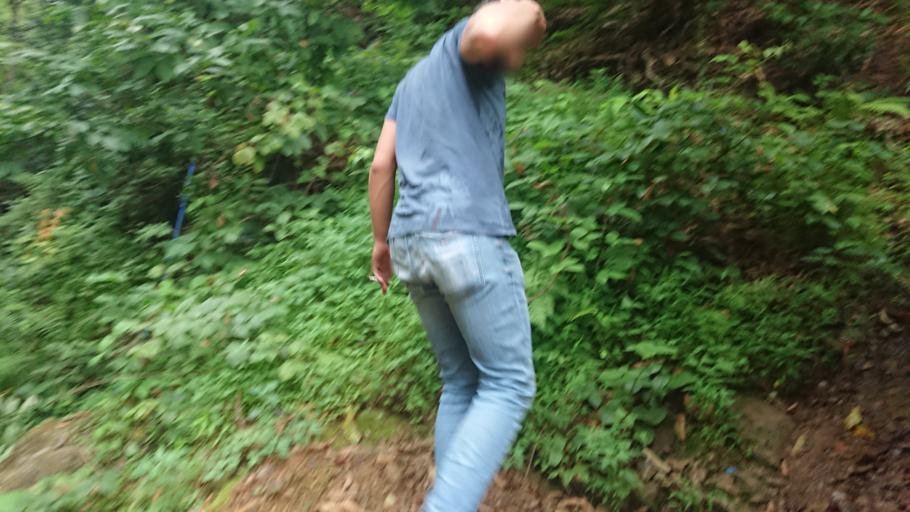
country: TR
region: Rize
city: Hemsin
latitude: 41.0461
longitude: 40.8084
